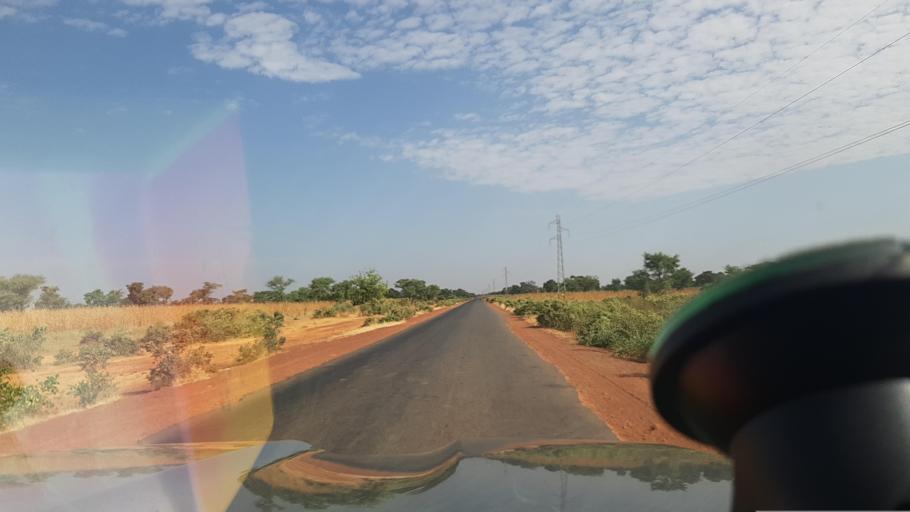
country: ML
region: Segou
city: Markala
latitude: 13.5533
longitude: -6.1156
